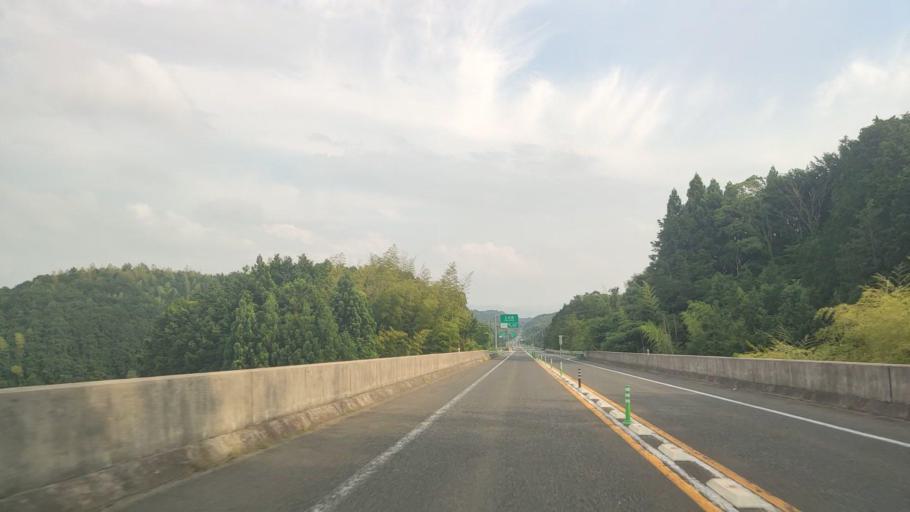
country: JP
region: Tottori
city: Kurayoshi
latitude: 35.4706
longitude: 133.8074
